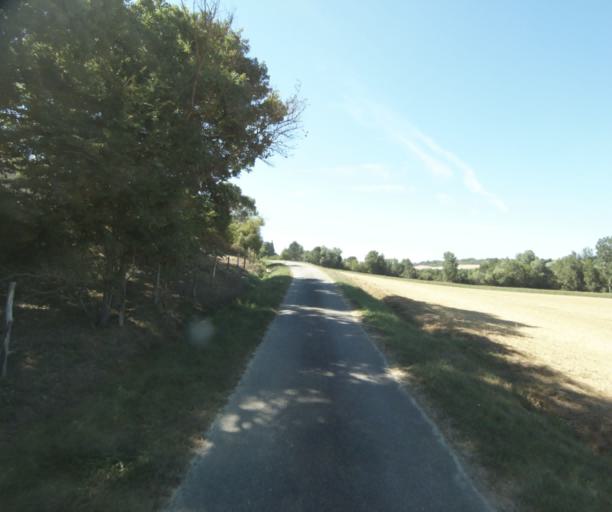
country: FR
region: Midi-Pyrenees
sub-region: Departement de la Haute-Garonne
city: Auriac-sur-Vendinelle
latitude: 43.5120
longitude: 1.8848
